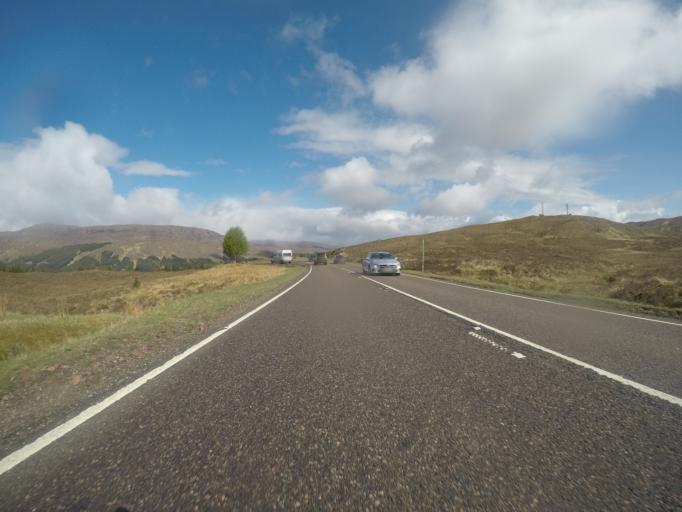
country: GB
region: Scotland
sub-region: Highland
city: Spean Bridge
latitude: 57.0964
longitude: -4.9950
